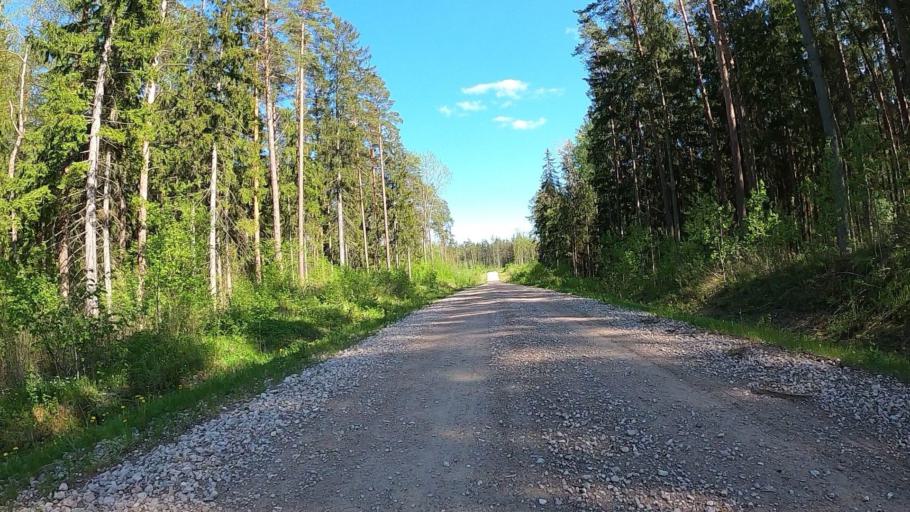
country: LV
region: Salaspils
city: Salaspils
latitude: 56.7906
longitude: 24.3352
